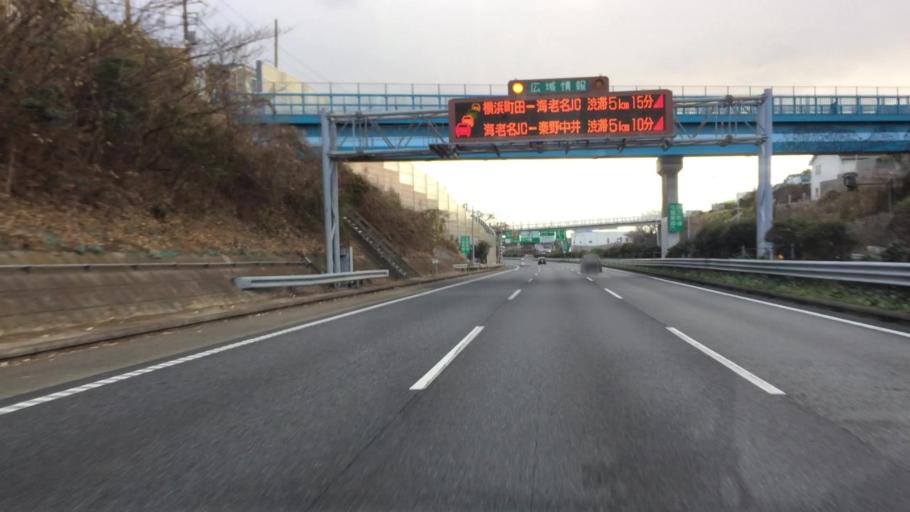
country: JP
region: Kanagawa
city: Yokohama
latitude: 35.4906
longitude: 139.5924
